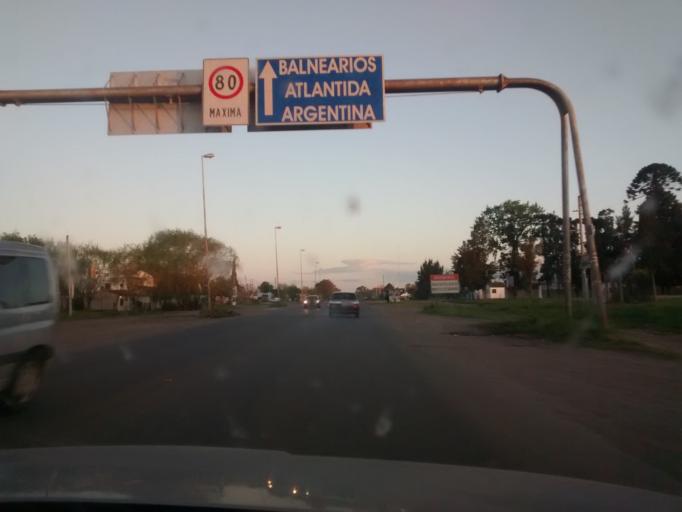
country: AR
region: Buenos Aires
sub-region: Partido de La Plata
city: La Plata
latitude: -34.9927
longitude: -58.0384
